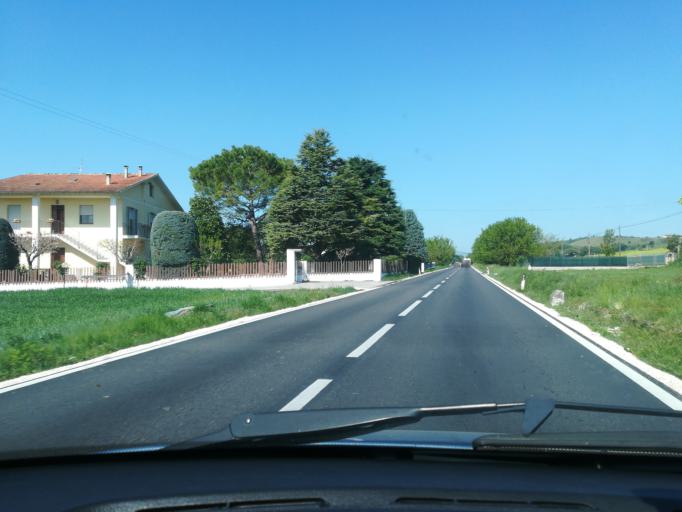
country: IT
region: The Marches
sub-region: Provincia di Macerata
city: Villa Potenza
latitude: 43.3246
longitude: 13.4118
